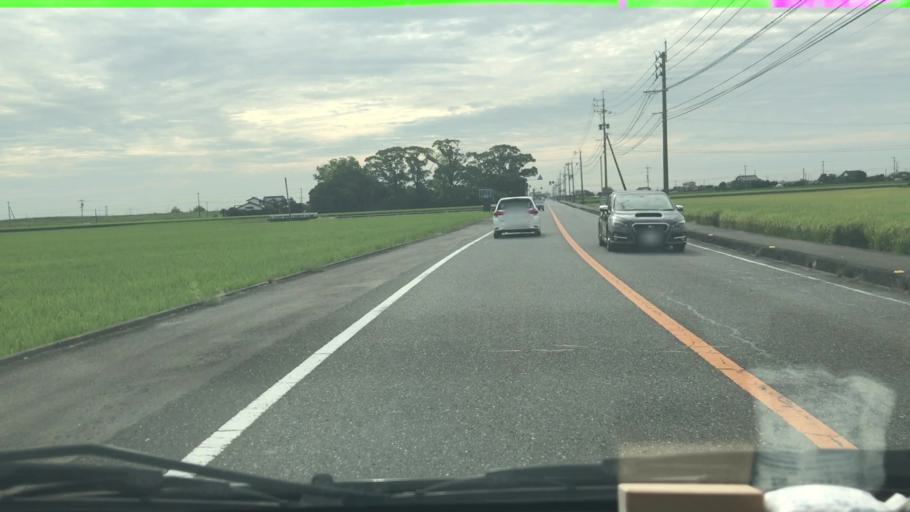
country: JP
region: Saga Prefecture
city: Takeocho-takeo
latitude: 33.2047
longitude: 130.0922
